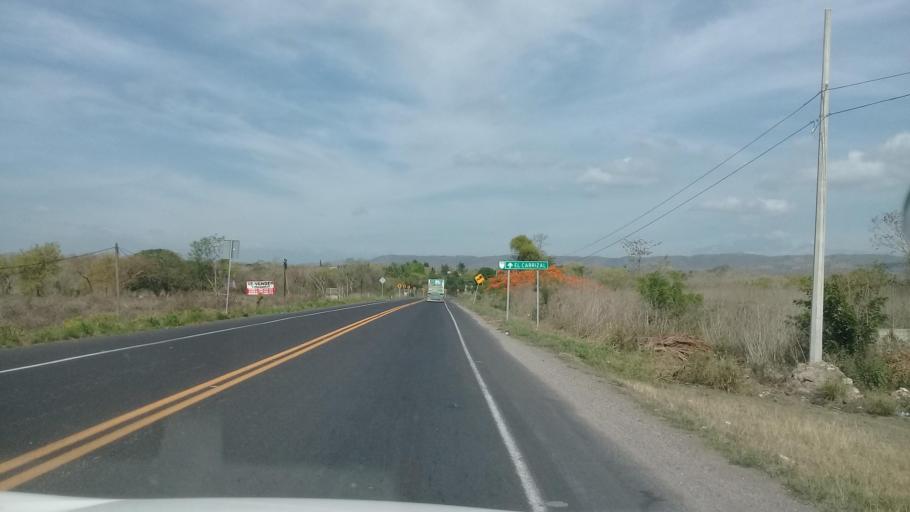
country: MX
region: Veracruz
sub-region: Emiliano Zapata
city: Plan del Rio
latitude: 19.3890
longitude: -96.6410
